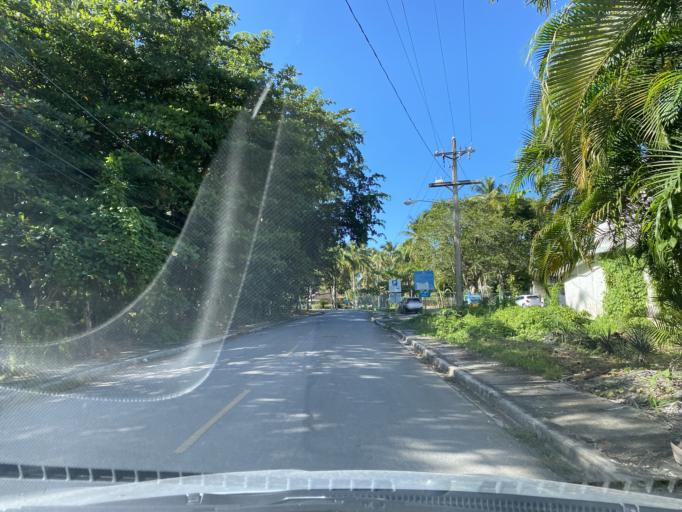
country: DO
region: Samana
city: Las Terrenas
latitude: 19.3123
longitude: -69.5720
